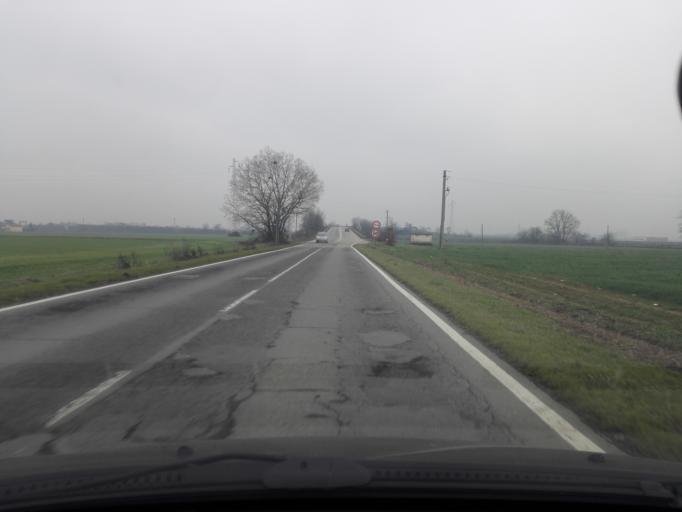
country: IT
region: Piedmont
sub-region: Provincia di Alessandria
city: Basaluzzo
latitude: 44.7946
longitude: 8.7302
